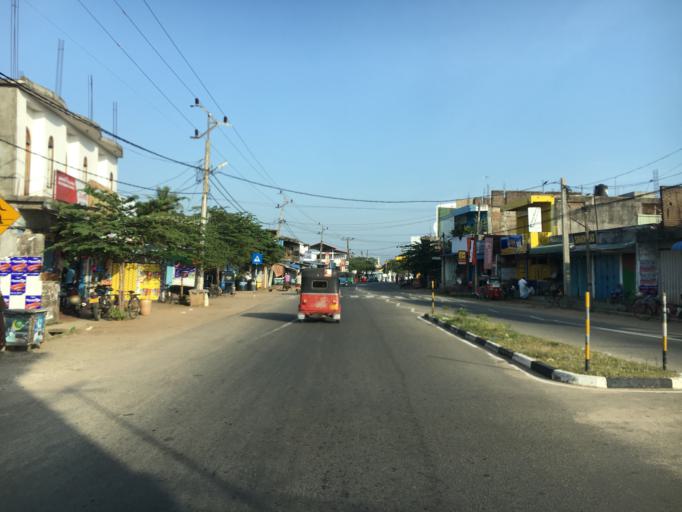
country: LK
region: Eastern Province
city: Eravur Town
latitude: 7.9158
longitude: 81.5211
